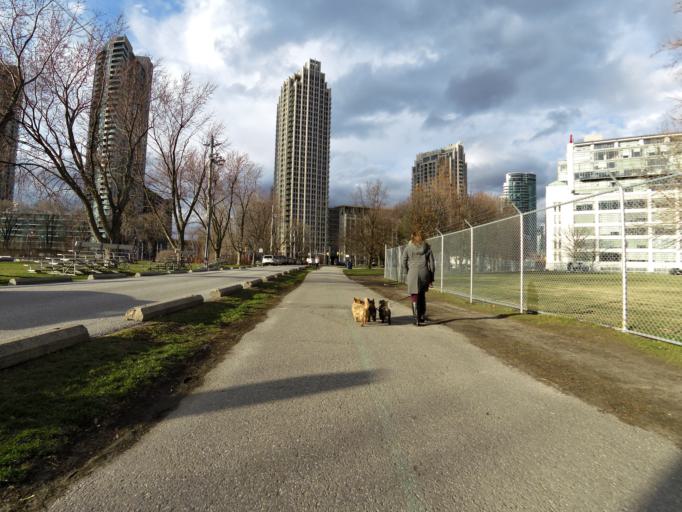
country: CA
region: Ontario
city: Toronto
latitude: 43.6344
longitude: -79.4040
